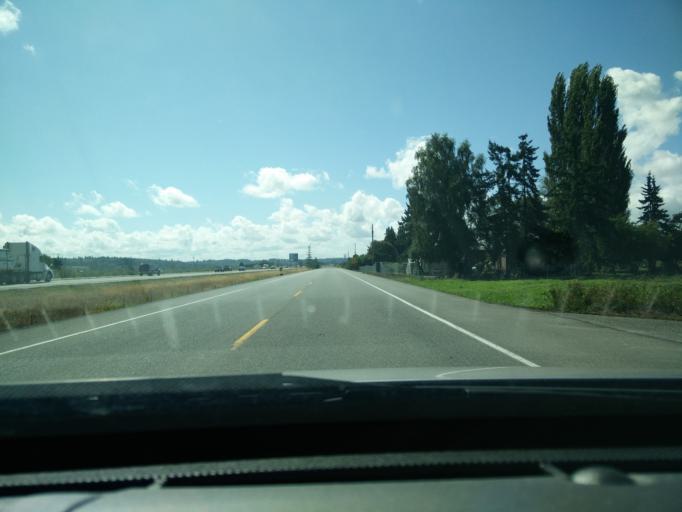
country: US
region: Washington
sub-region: Skagit County
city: Mount Vernon
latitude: 48.3595
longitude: -122.3365
